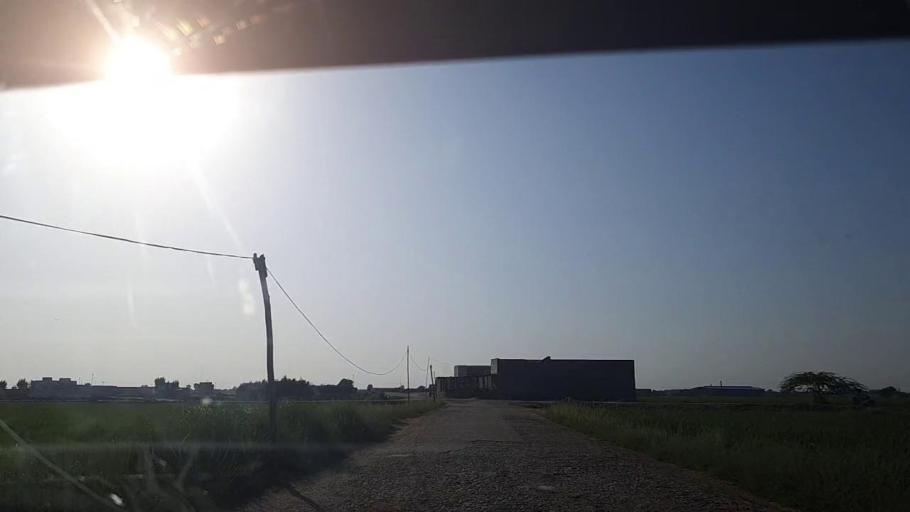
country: PK
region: Sindh
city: Tangwani
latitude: 28.2610
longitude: 69.0083
